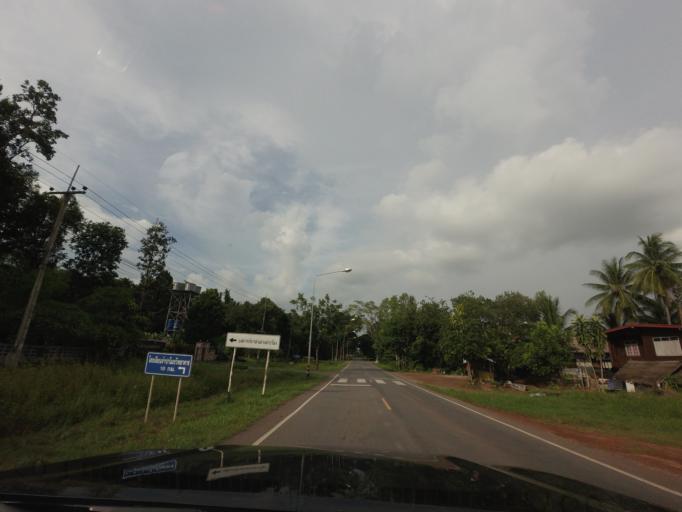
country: TH
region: Changwat Nong Bua Lamphu
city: Suwannakhuha
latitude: 17.5551
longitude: 102.3918
